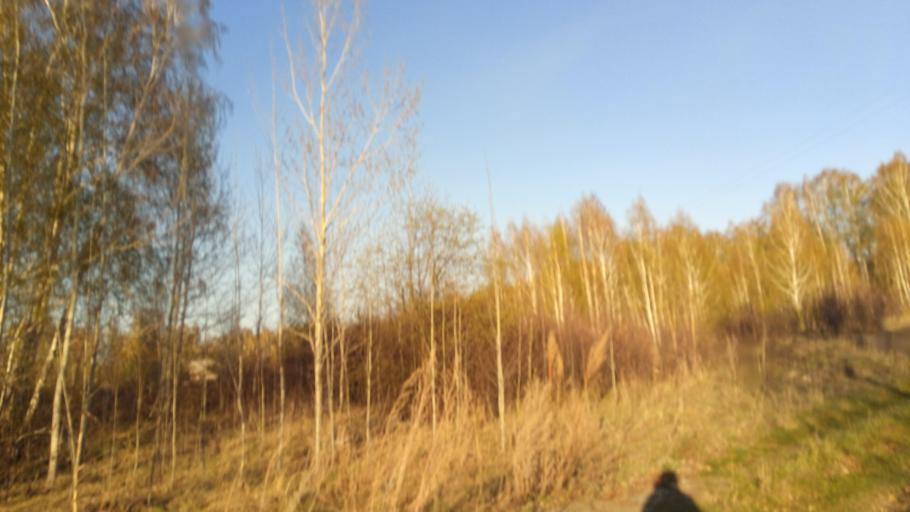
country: RU
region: Chelyabinsk
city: Timiryazevskiy
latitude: 54.9915
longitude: 60.8632
